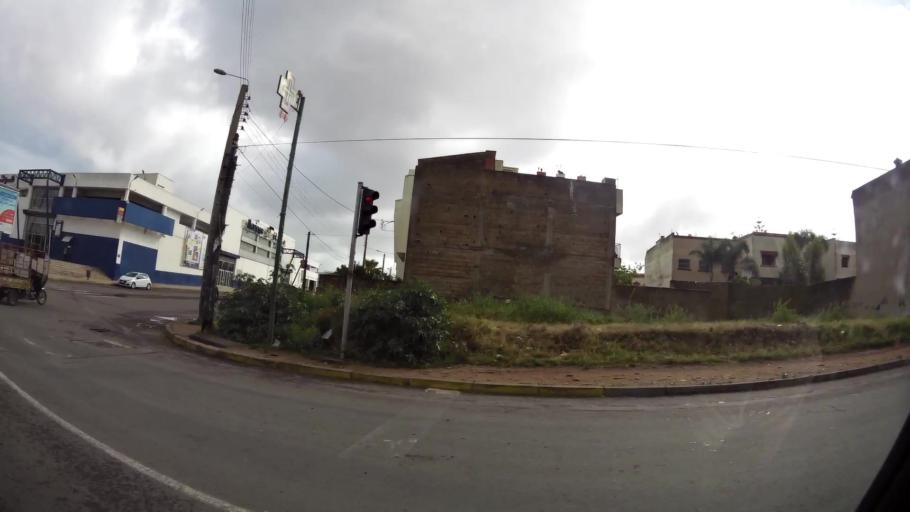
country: MA
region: Grand Casablanca
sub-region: Casablanca
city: Casablanca
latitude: 33.5656
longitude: -7.6767
